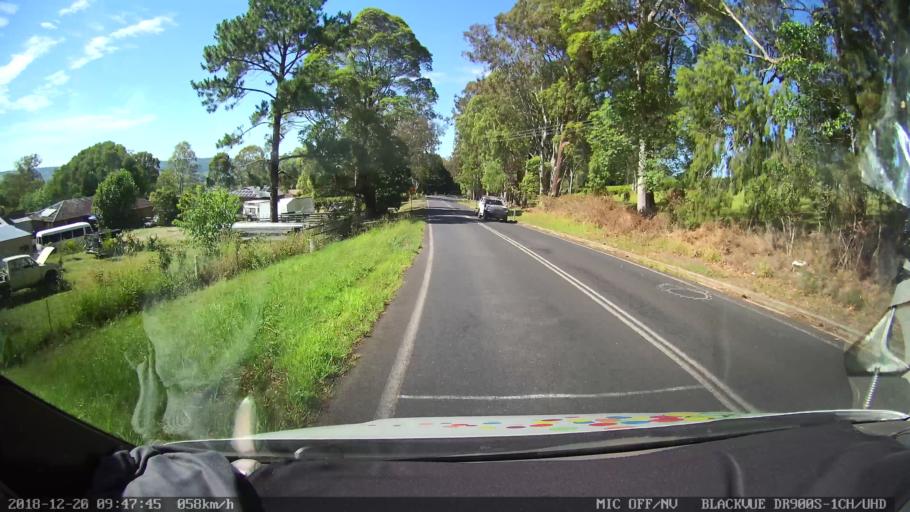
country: AU
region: New South Wales
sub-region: Lismore Municipality
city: Lismore
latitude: -28.7658
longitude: 153.2951
